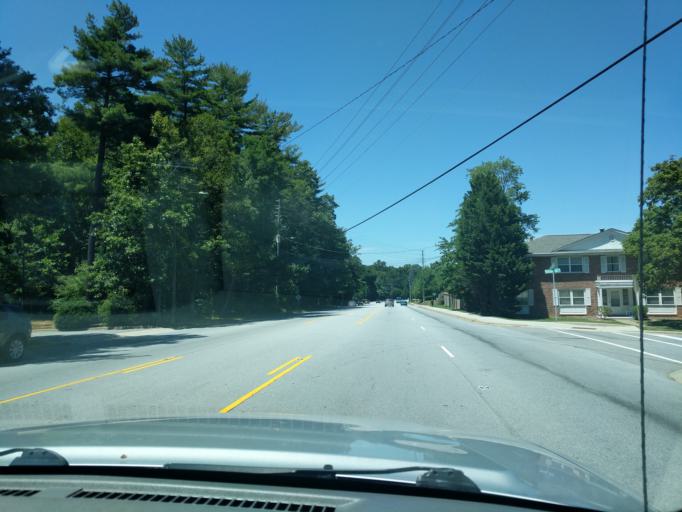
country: US
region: North Carolina
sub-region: Buncombe County
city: Biltmore Forest
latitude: 35.5373
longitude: -82.5296
